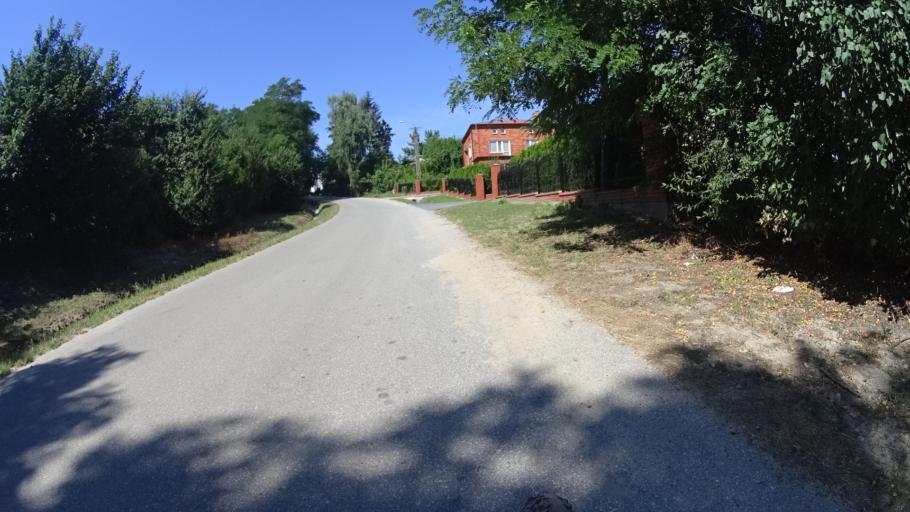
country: PL
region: Masovian Voivodeship
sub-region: Powiat bialobrzeski
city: Bialobrzegi
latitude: 51.6670
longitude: 20.9175
